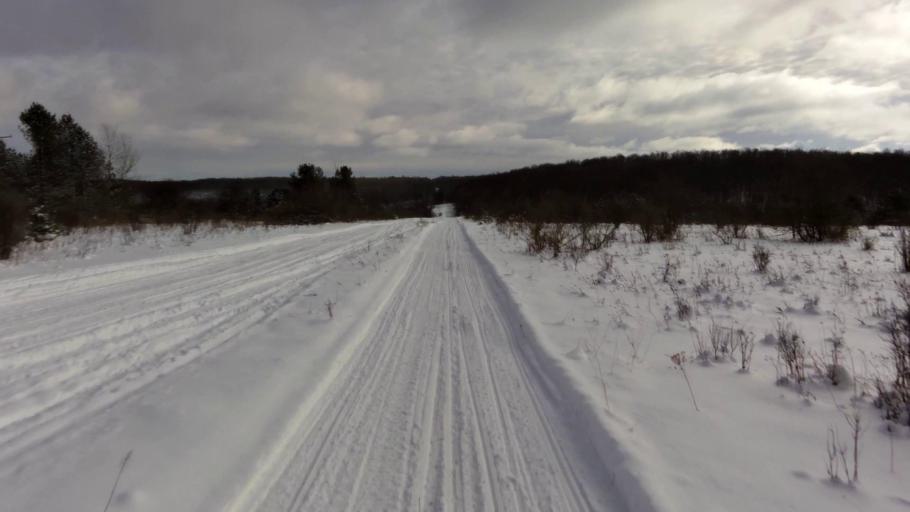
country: US
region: New York
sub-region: Cattaraugus County
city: Franklinville
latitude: 42.3144
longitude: -78.5371
